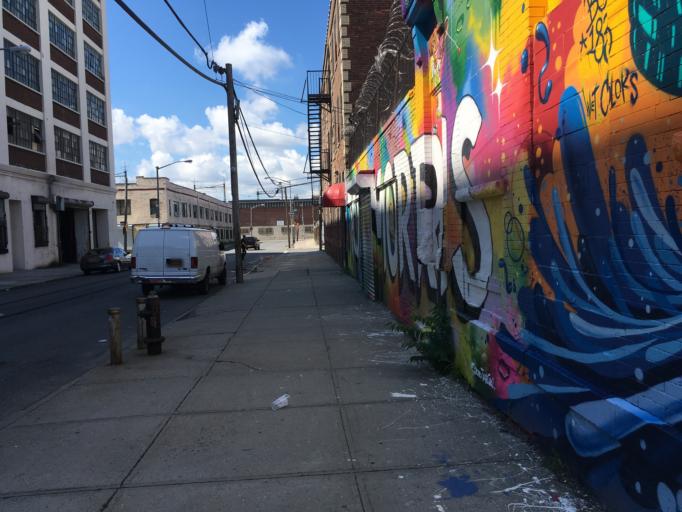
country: US
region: New York
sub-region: New York County
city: Manhattan
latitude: 40.8015
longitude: -73.9133
